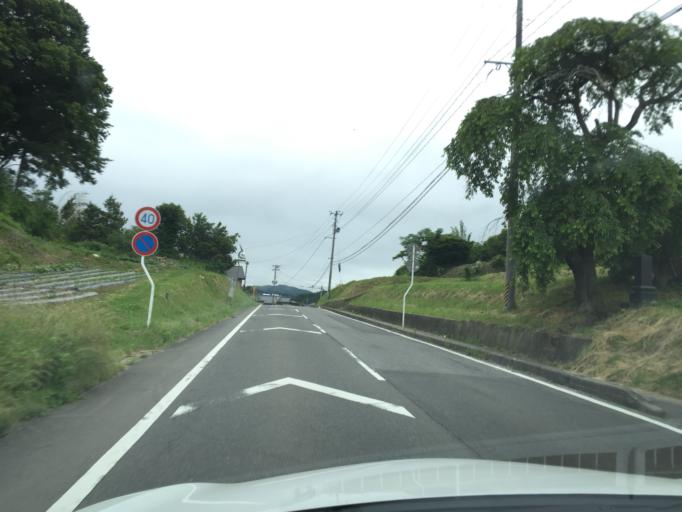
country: JP
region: Fukushima
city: Funehikimachi-funehiki
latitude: 37.3299
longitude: 140.6575
